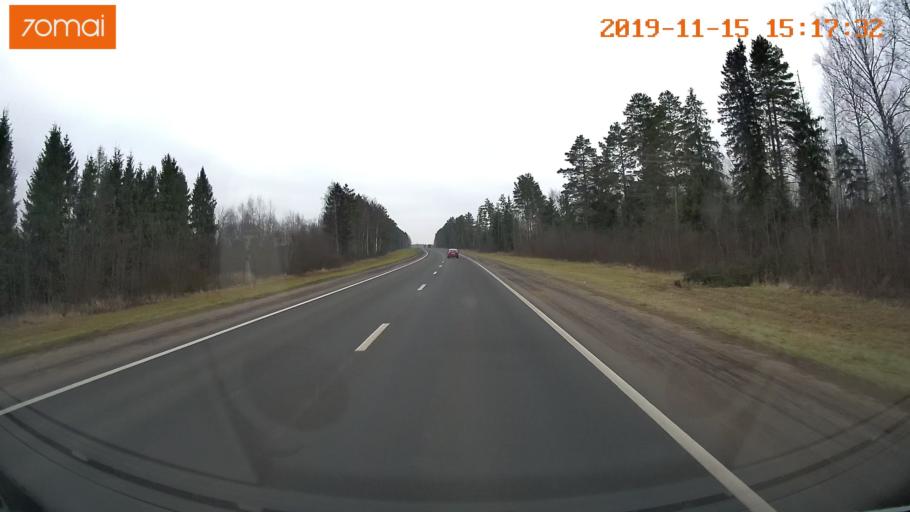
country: RU
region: Jaroslavl
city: Danilov
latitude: 58.2596
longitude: 40.1812
